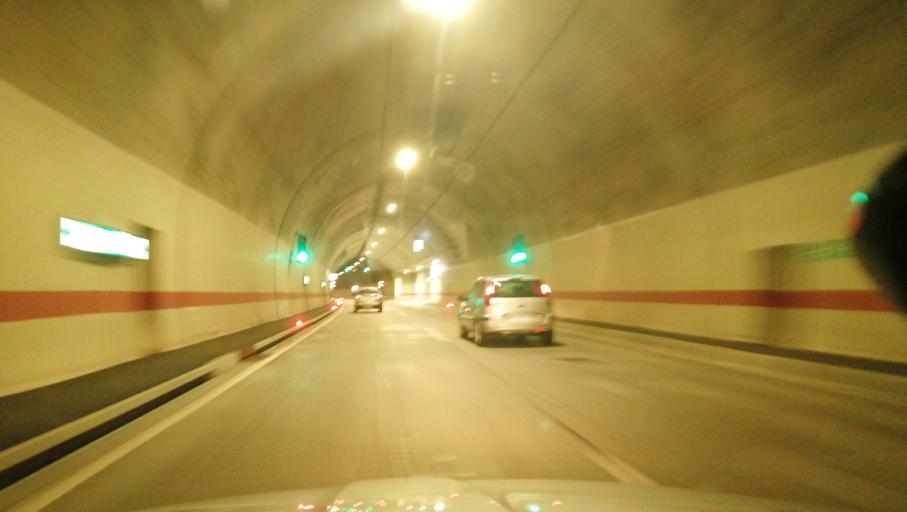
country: RS
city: Prislonica
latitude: 44.0111
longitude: 20.3708
